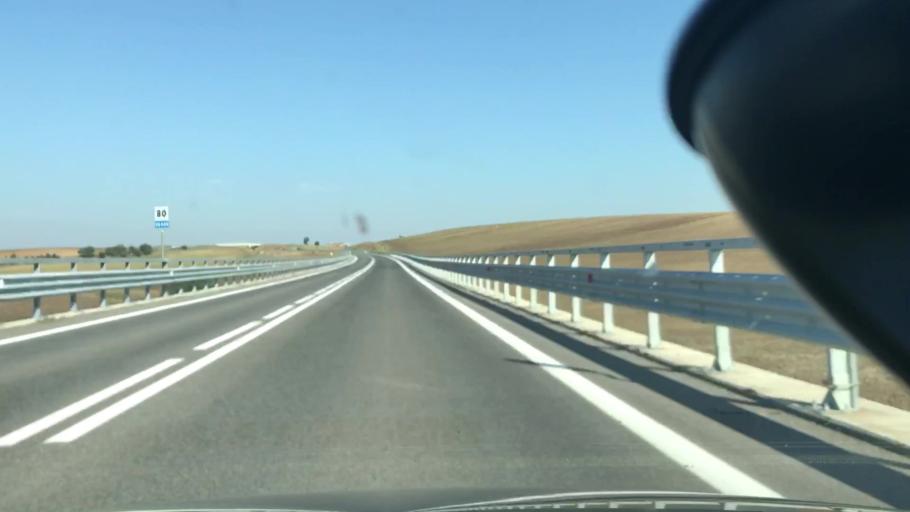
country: IT
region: Basilicate
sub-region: Provincia di Potenza
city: Palazzo San Gervasio
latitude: 40.9622
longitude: 16.0120
